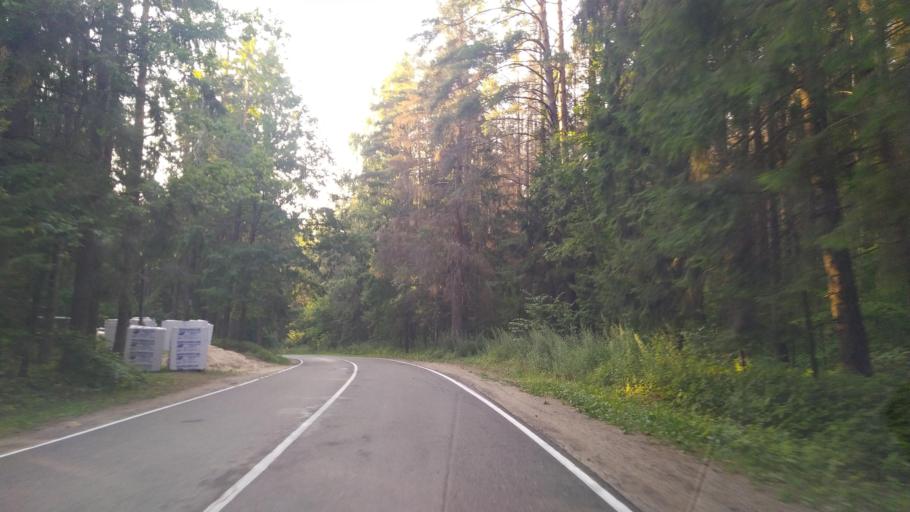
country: RU
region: Pskov
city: Pushkinskiye Gory
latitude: 57.0337
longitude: 28.9191
